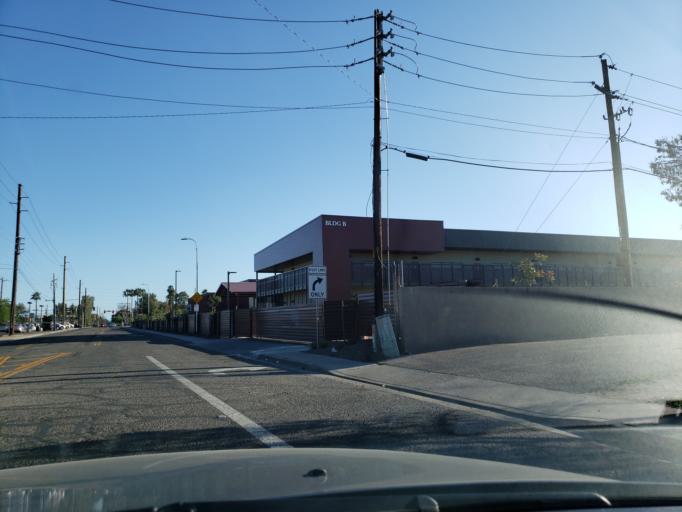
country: US
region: Arizona
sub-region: Maricopa County
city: Glendale
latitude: 33.5404
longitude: -112.1558
